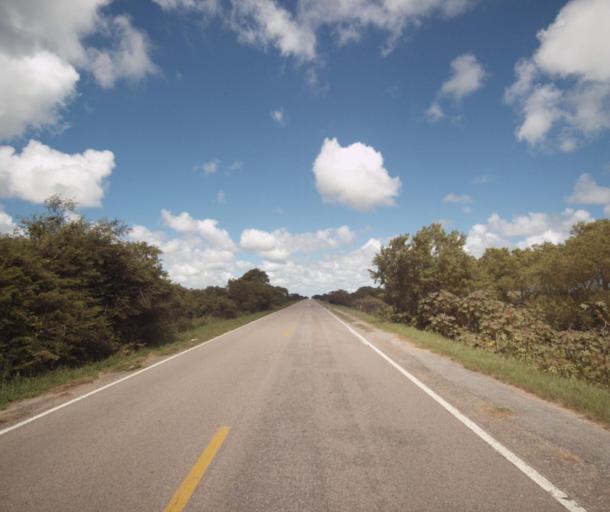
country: BR
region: Rio Grande do Sul
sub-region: Arroio Grande
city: Arroio Grande
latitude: -32.5494
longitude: -52.5456
